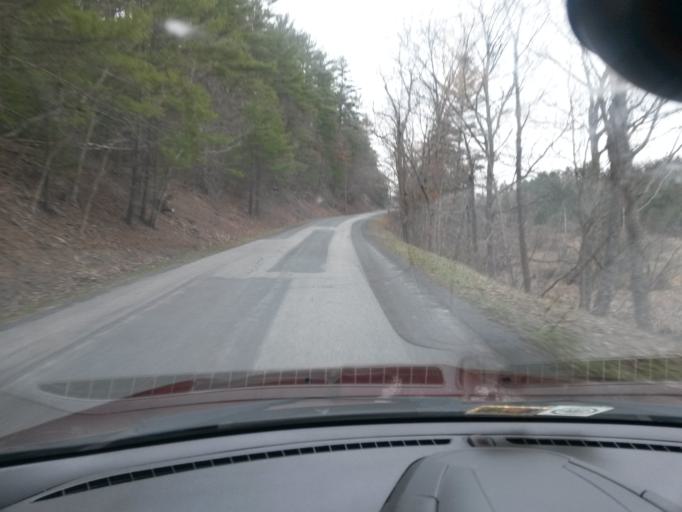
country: US
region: Virginia
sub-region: Bath County
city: Warm Springs
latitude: 38.0354
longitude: -79.8573
